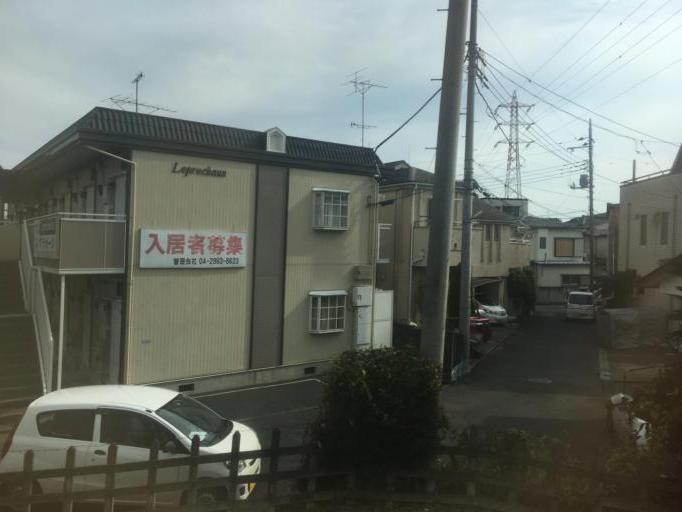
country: JP
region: Saitama
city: Sayama
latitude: 35.8181
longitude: 139.4134
